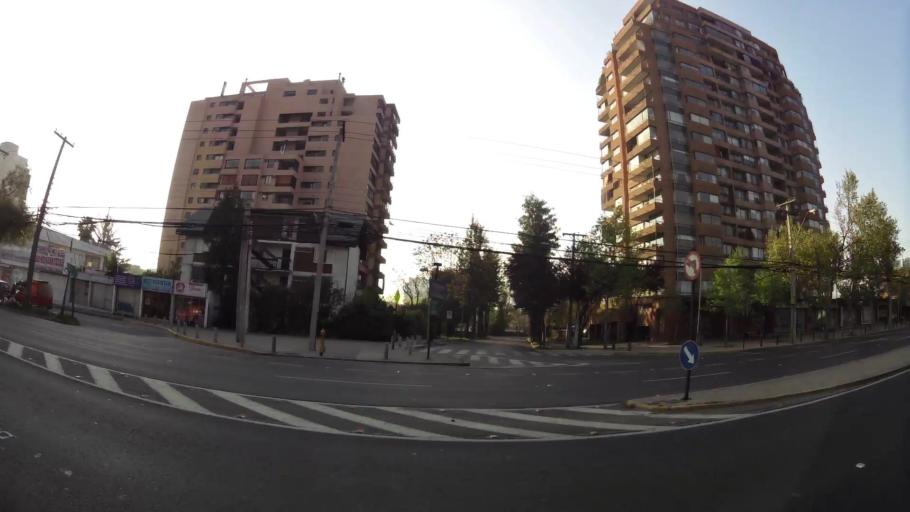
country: CL
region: Santiago Metropolitan
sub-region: Provincia de Santiago
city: Villa Presidente Frei, Nunoa, Santiago, Chile
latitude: -33.3914
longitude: -70.5419
